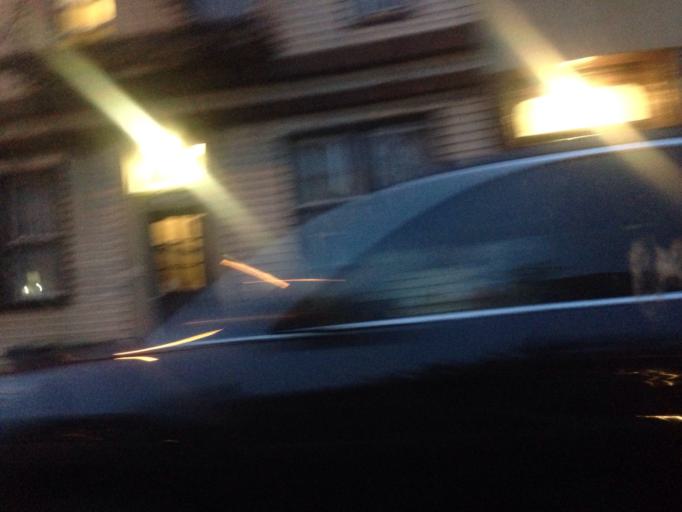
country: US
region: New York
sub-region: Queens County
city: Long Island City
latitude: 40.7303
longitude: -73.9528
